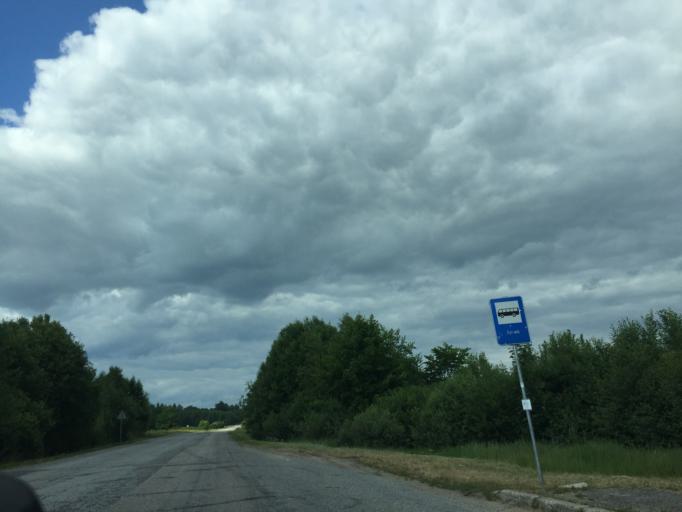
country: LV
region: Skriveri
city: Skriveri
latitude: 56.8224
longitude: 25.1215
